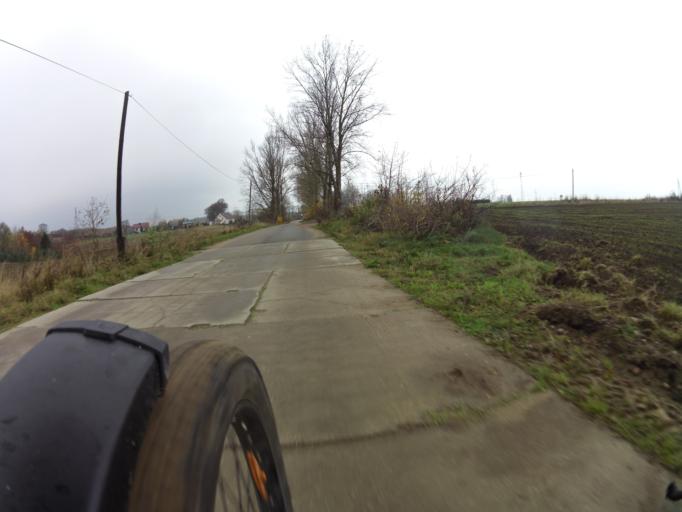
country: PL
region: Pomeranian Voivodeship
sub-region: Powiat pucki
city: Krokowa
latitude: 54.7205
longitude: 18.1382
